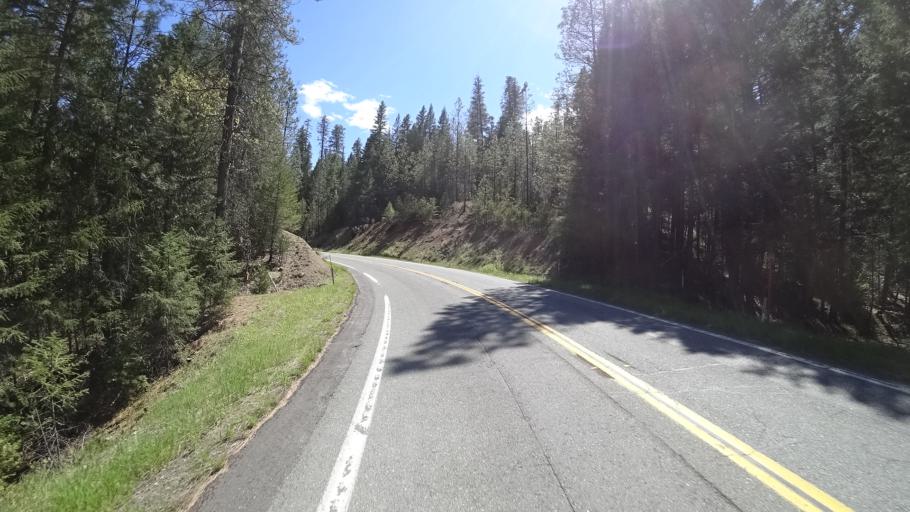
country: US
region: California
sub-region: Trinity County
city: Lewiston
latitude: 40.8653
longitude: -122.8183
